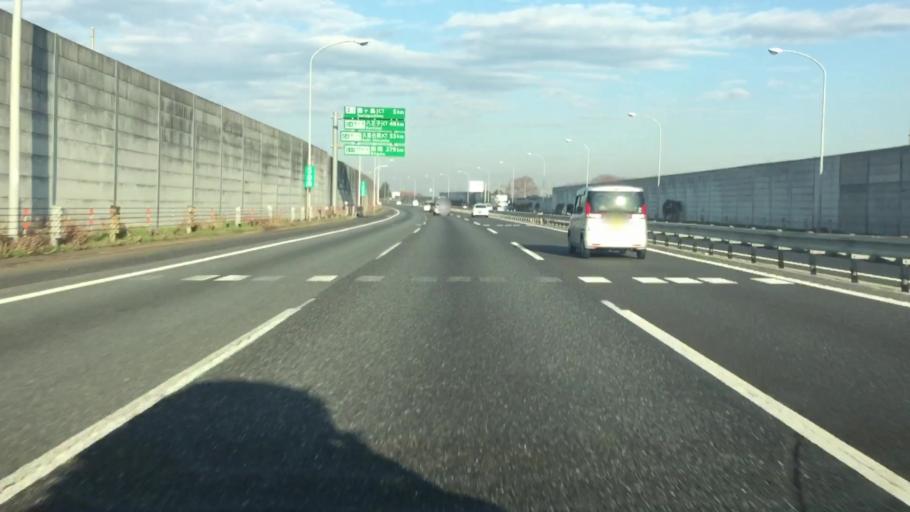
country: JP
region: Saitama
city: Kawagoe
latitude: 35.9047
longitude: 139.4515
